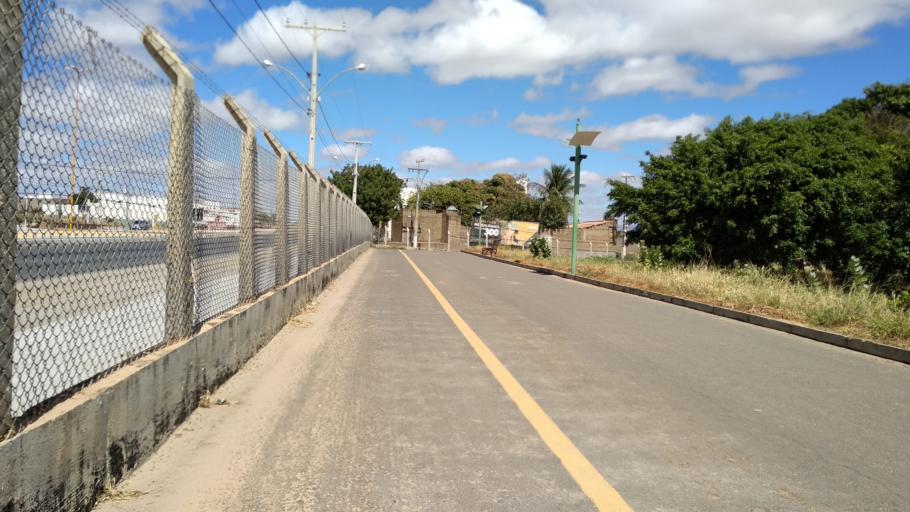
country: BR
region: Bahia
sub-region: Guanambi
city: Guanambi
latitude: -14.2262
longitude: -42.7642
